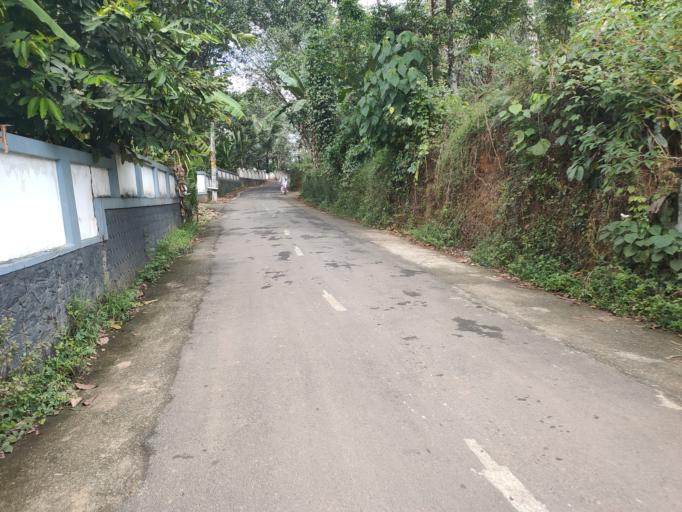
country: IN
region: Kerala
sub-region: Ernakulam
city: Kotamangalam
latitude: 10.0010
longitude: 76.6456
